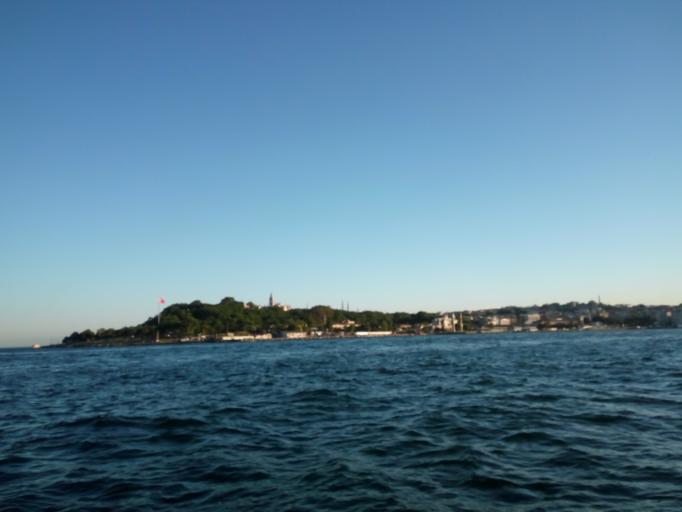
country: TR
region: Istanbul
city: Eminoenue
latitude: 41.0219
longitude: 28.9863
